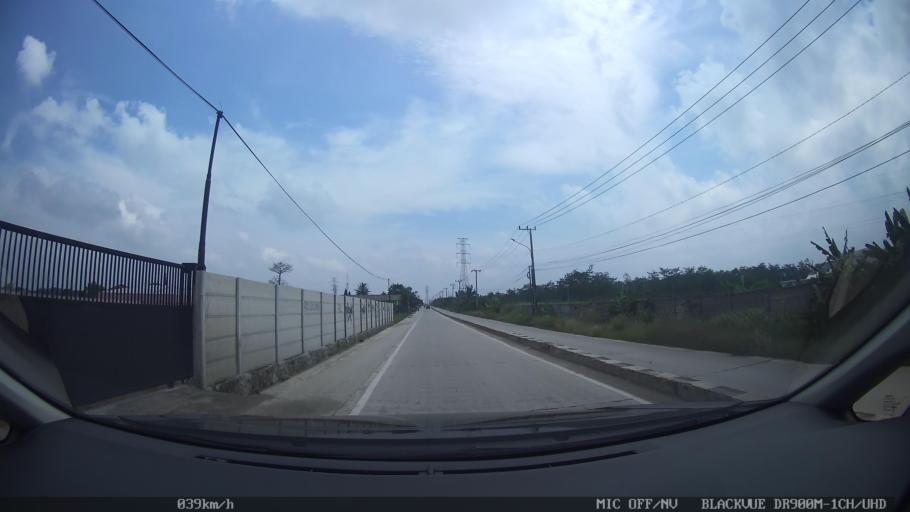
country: ID
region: Lampung
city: Kedaton
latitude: -5.3689
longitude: 105.3084
